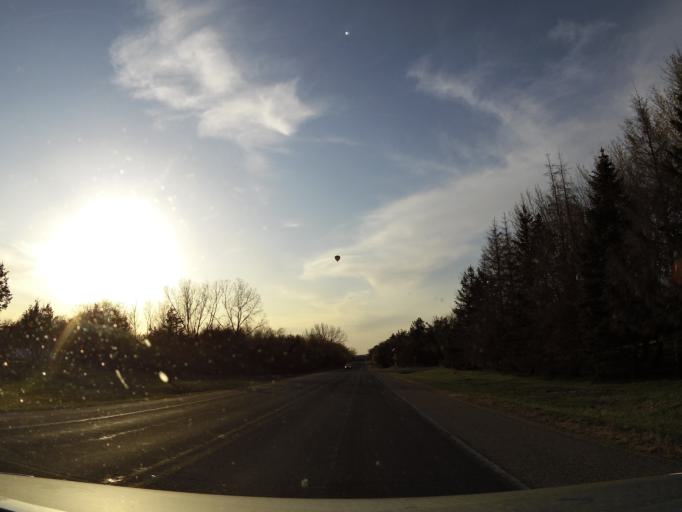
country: US
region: Minnesota
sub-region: Washington County
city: Lakeland
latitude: 44.9379
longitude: -92.7226
